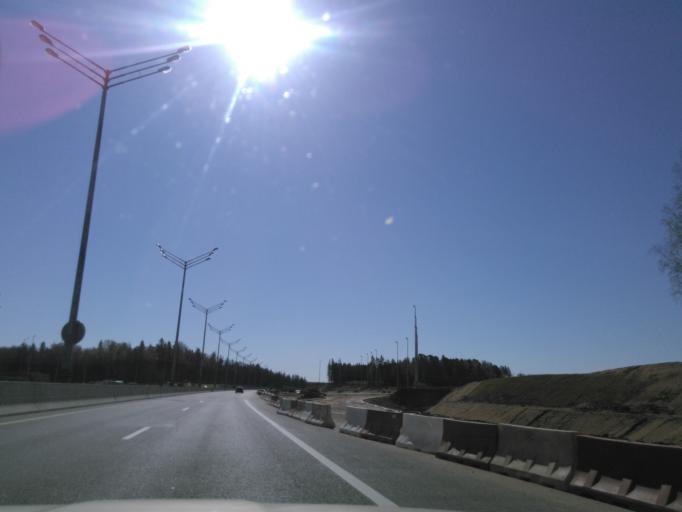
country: RU
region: Moskovskaya
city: Radumlya
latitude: 56.0973
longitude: 37.1813
